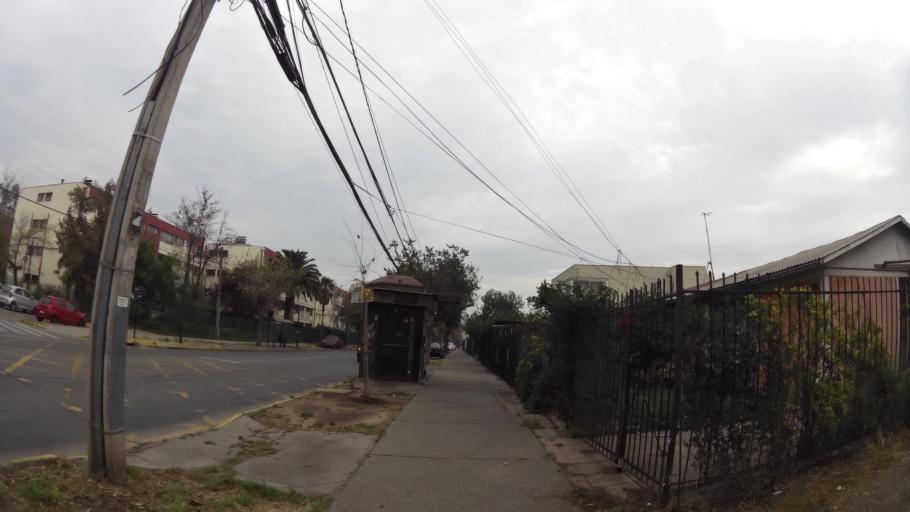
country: CL
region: Santiago Metropolitan
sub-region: Provincia de Santiago
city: Villa Presidente Frei, Nunoa, Santiago, Chile
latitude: -33.4700
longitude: -70.5823
